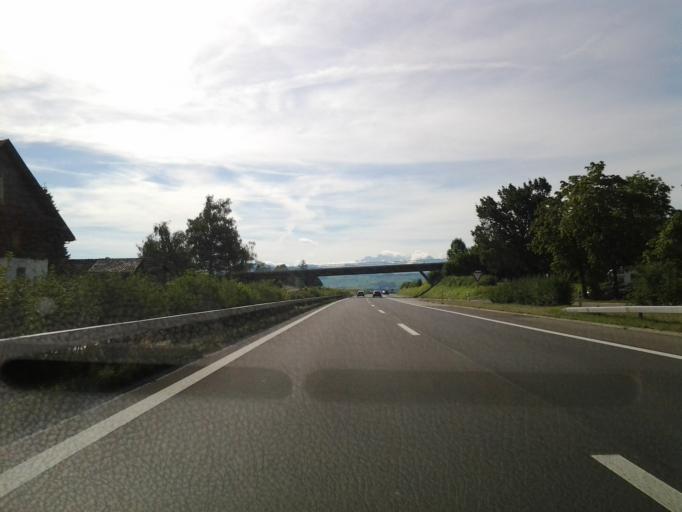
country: CH
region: Zurich
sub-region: Bezirk Horgen
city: Waedenswil / Untermosen-Fuhr
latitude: 47.2197
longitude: 8.6621
